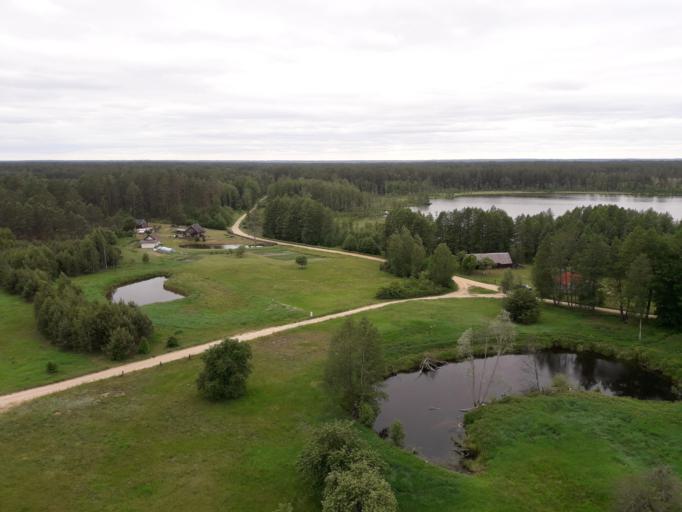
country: LT
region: Alytaus apskritis
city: Druskininkai
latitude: 54.0381
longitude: 24.1825
